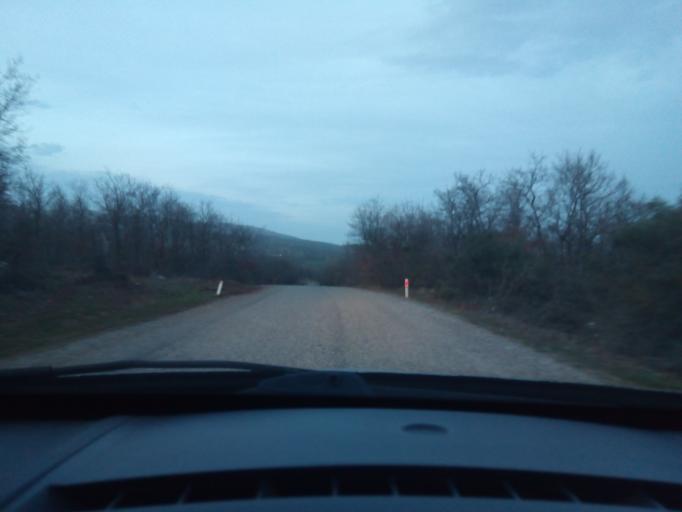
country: TR
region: Balikesir
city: Omerkoy
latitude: 39.9210
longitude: 28.0609
